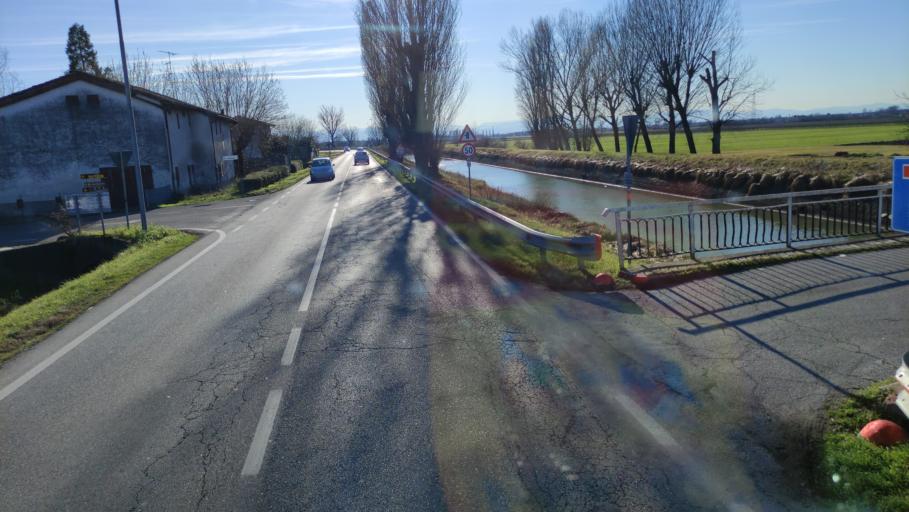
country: IT
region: Emilia-Romagna
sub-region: Provincia di Reggio Emilia
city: Novellara
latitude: 44.8317
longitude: 10.7093
